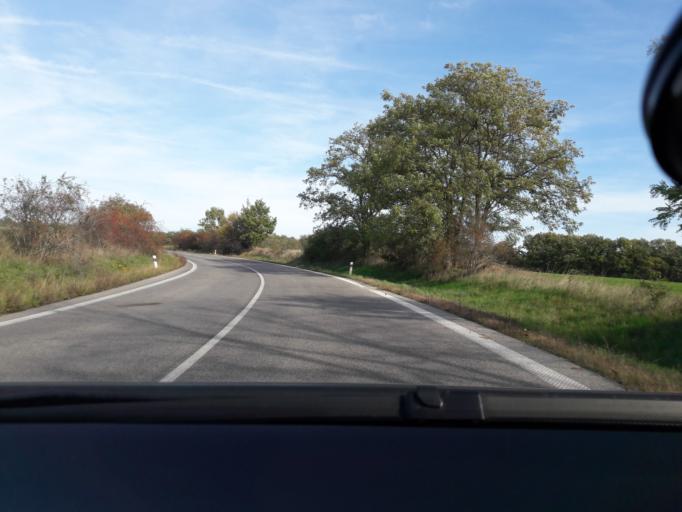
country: SK
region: Banskobystricky
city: Dudince
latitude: 48.2560
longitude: 18.7667
